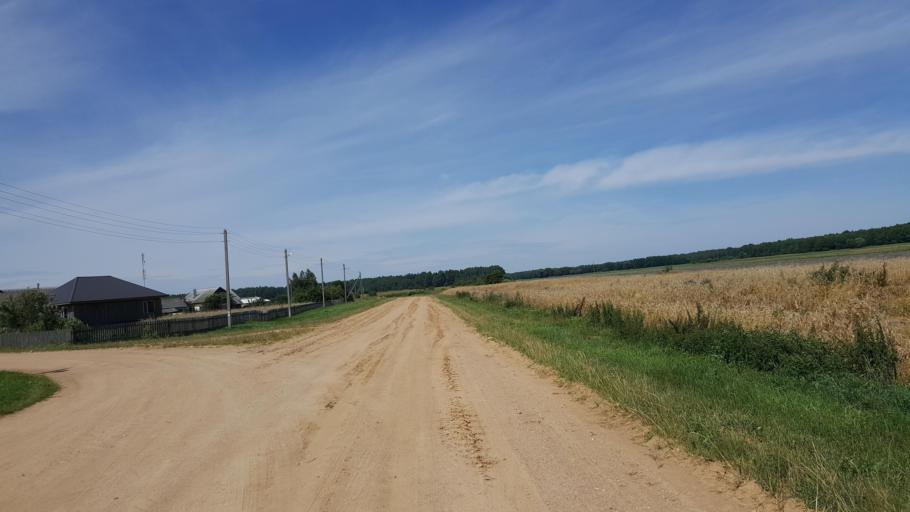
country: BY
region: Brest
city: Pruzhany
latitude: 52.5642
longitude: 24.2270
